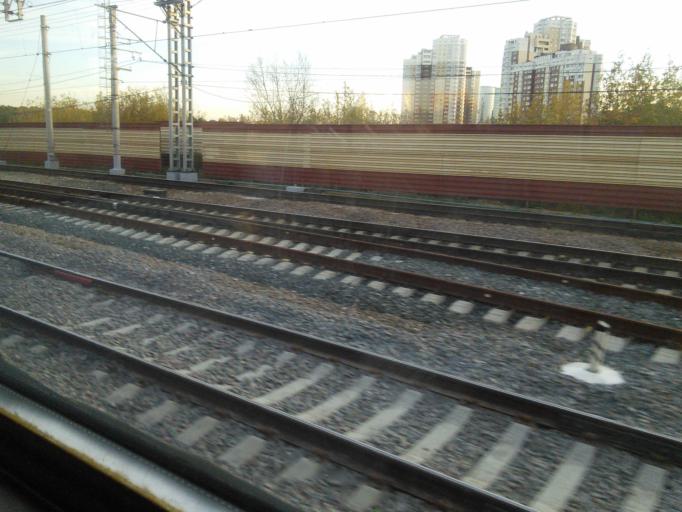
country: RU
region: Moskovskaya
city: Levoberezhnaya
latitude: 55.8911
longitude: 37.4592
